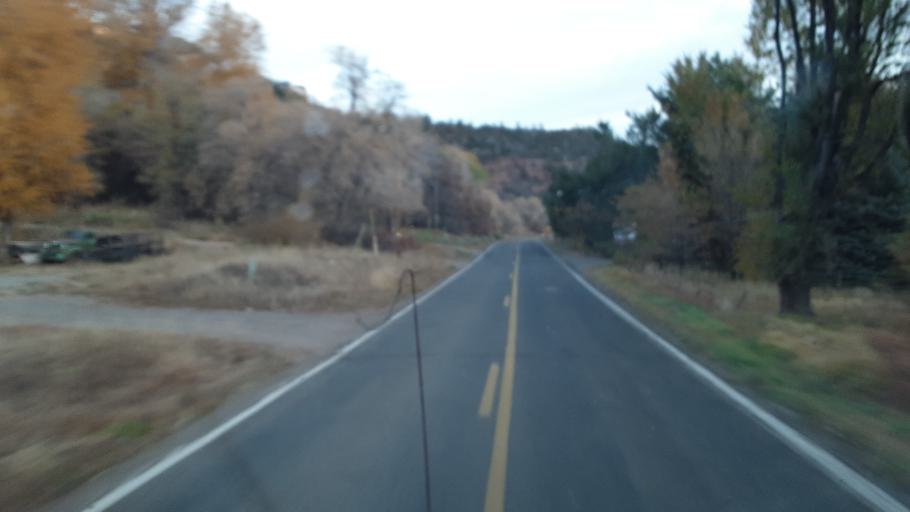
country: US
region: Colorado
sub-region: La Plata County
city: Durango
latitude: 37.3457
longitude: -107.8568
